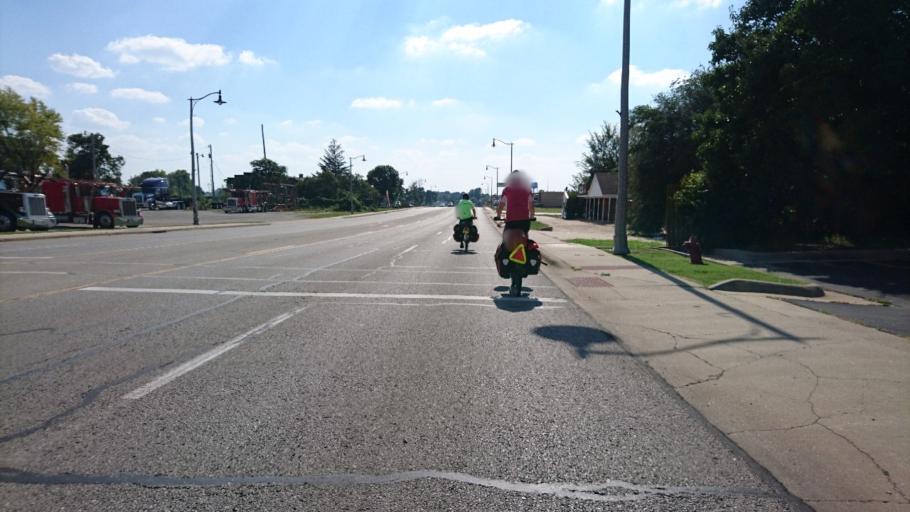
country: US
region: Missouri
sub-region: Laclede County
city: Lebanon
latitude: 37.6730
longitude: -92.6621
